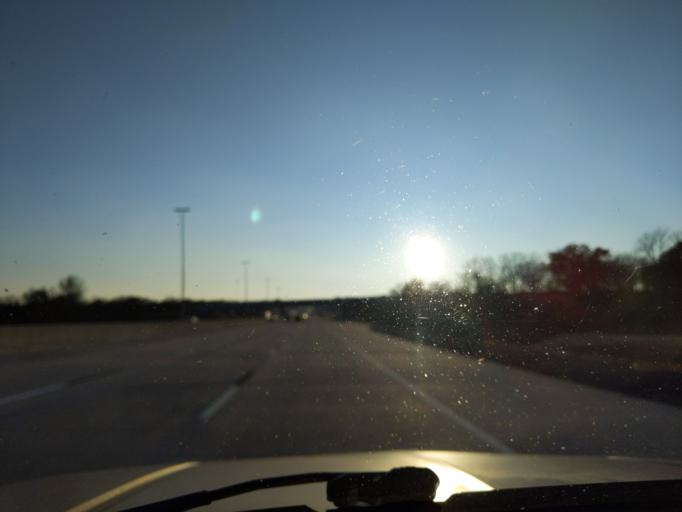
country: US
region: Oklahoma
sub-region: Creek County
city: Kellyville
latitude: 35.9658
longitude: -96.2241
